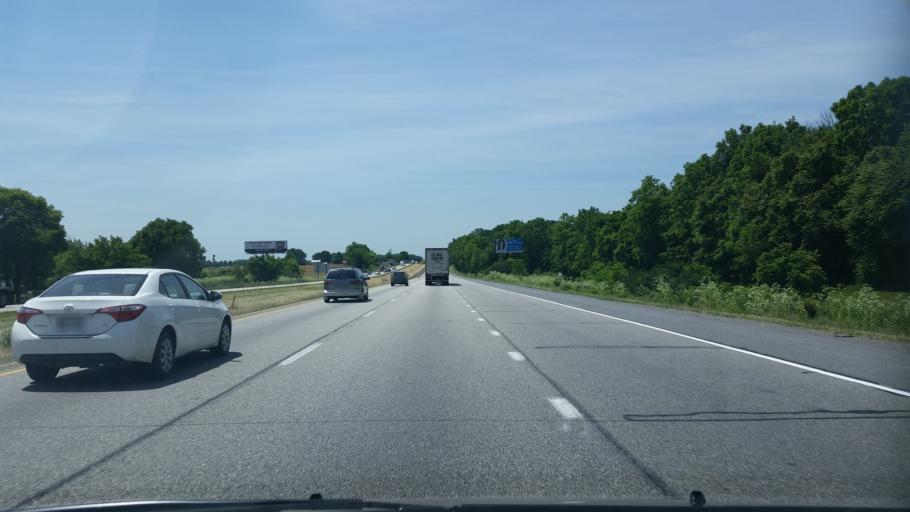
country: US
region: Pennsylvania
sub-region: Franklin County
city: Greencastle
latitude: 39.7835
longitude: -77.7144
